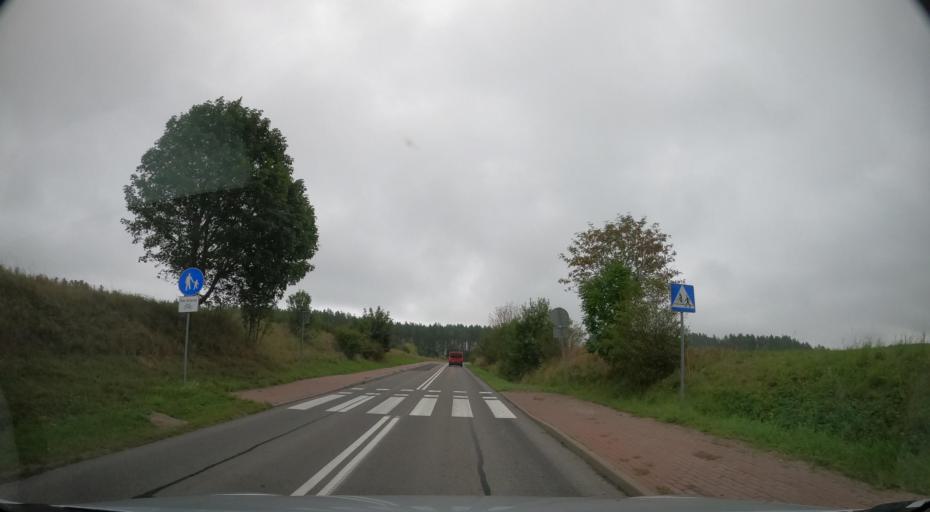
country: PL
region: Pomeranian Voivodeship
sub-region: Powiat wejherowski
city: Linia
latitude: 54.4573
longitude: 18.0049
